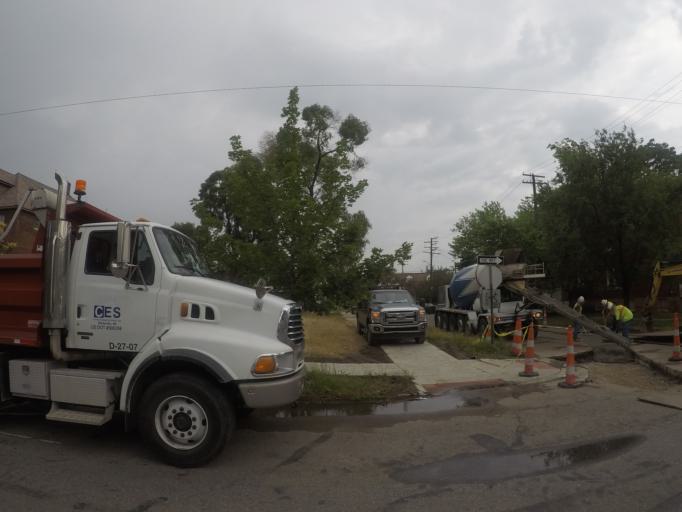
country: US
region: Michigan
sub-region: Wayne County
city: River Rouge
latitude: 42.3104
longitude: -83.1062
